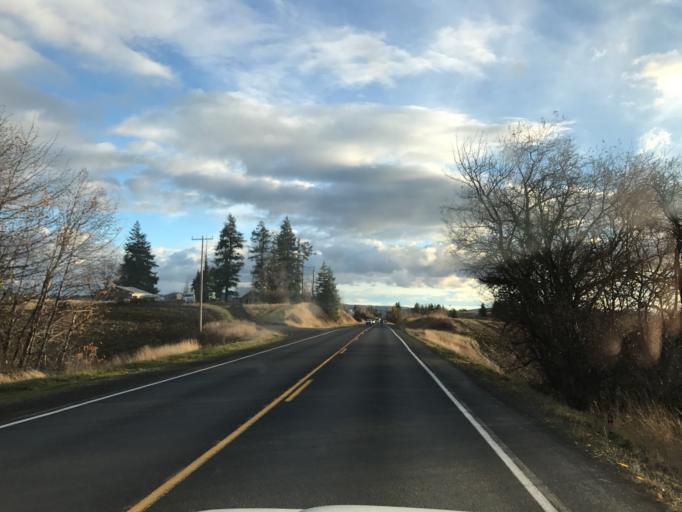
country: US
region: Idaho
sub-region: Latah County
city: Moscow
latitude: 46.7626
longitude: -117.0017
